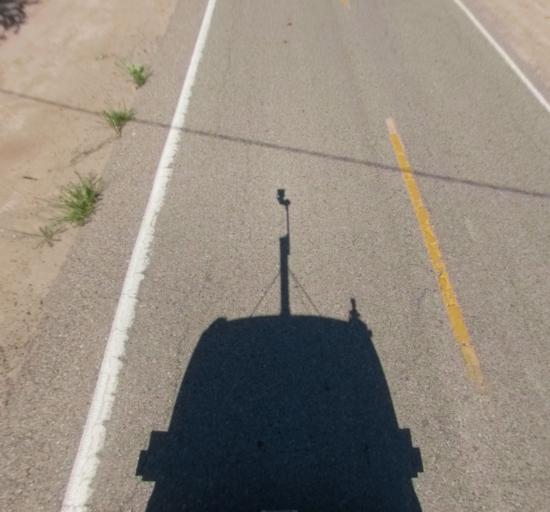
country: US
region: California
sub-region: Fresno County
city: Firebaugh
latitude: 37.0182
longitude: -120.4230
